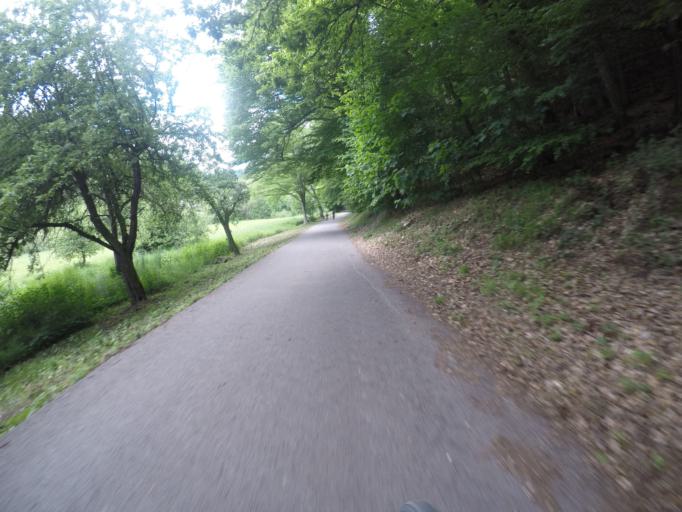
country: DE
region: Baden-Wuerttemberg
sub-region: Karlsruhe Region
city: Unterreichenbach
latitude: 48.8360
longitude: 8.7002
